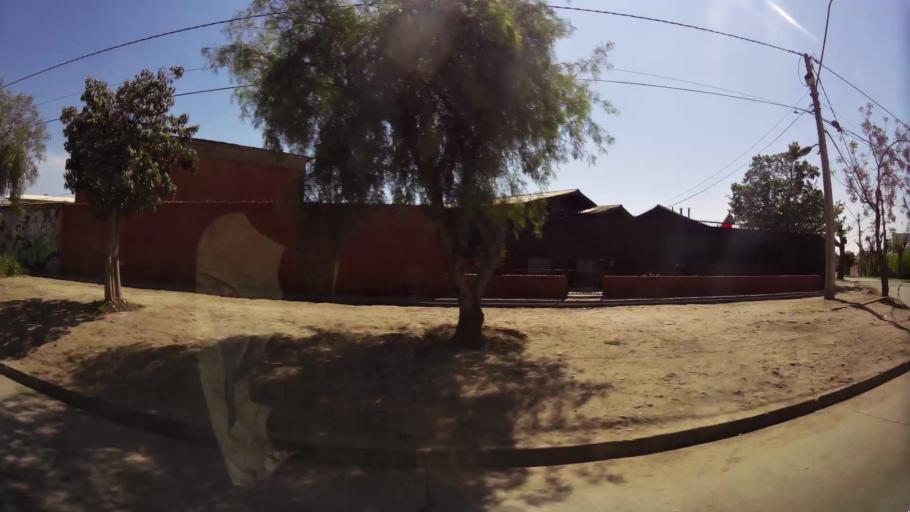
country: CL
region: Santiago Metropolitan
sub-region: Provincia de Santiago
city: Lo Prado
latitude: -33.5184
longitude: -70.7469
